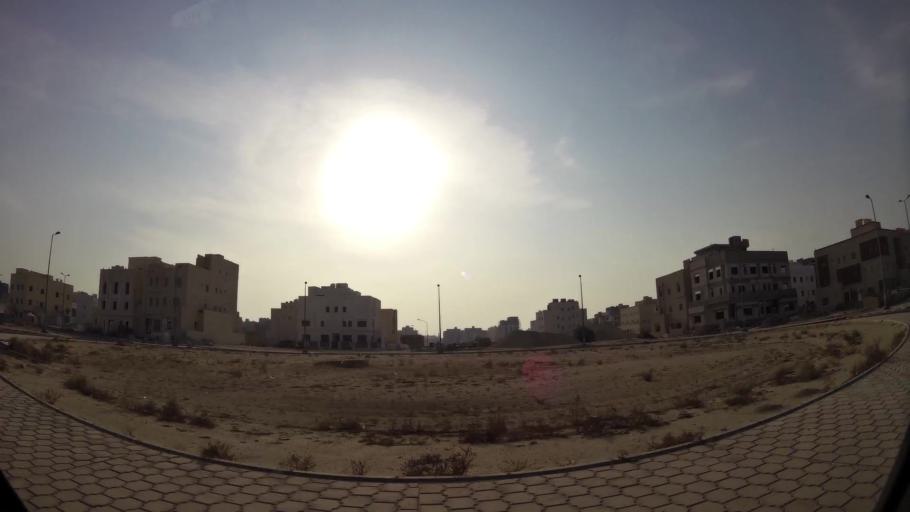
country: KW
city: Al Funaytis
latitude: 29.2257
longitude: 48.0916
